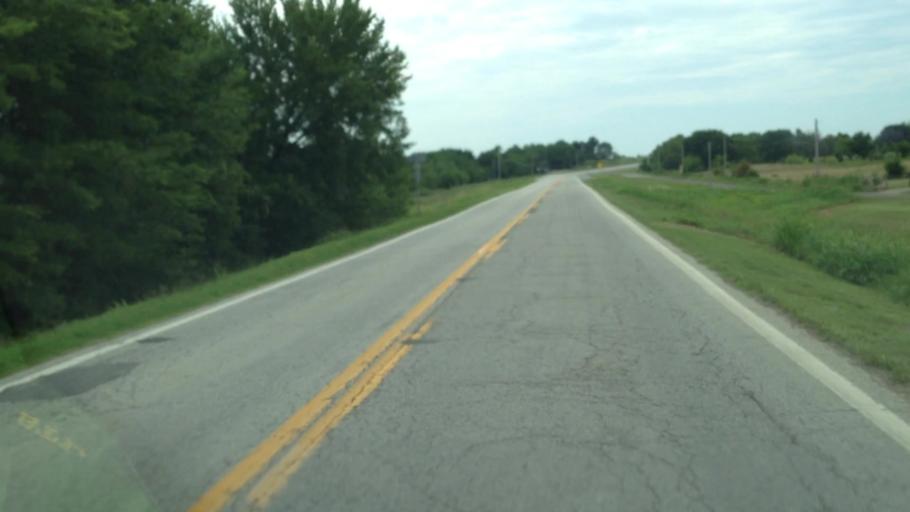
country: US
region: Kansas
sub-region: Labette County
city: Chetopa
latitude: 36.8820
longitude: -95.0989
